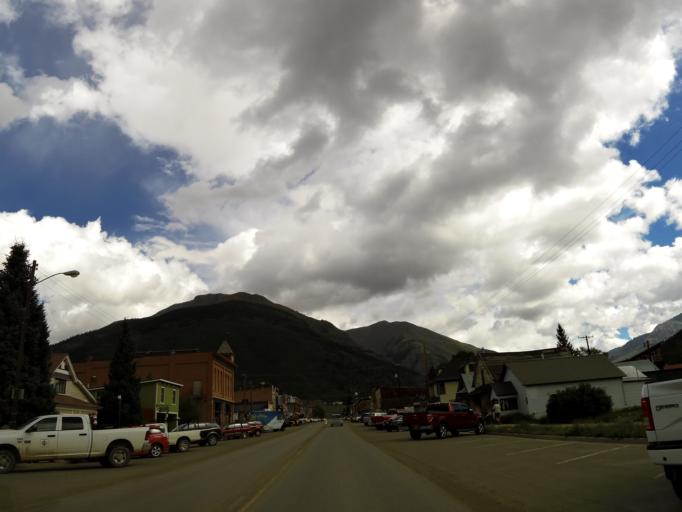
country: US
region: Colorado
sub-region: San Juan County
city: Silverton
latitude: 37.8101
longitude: -107.6658
